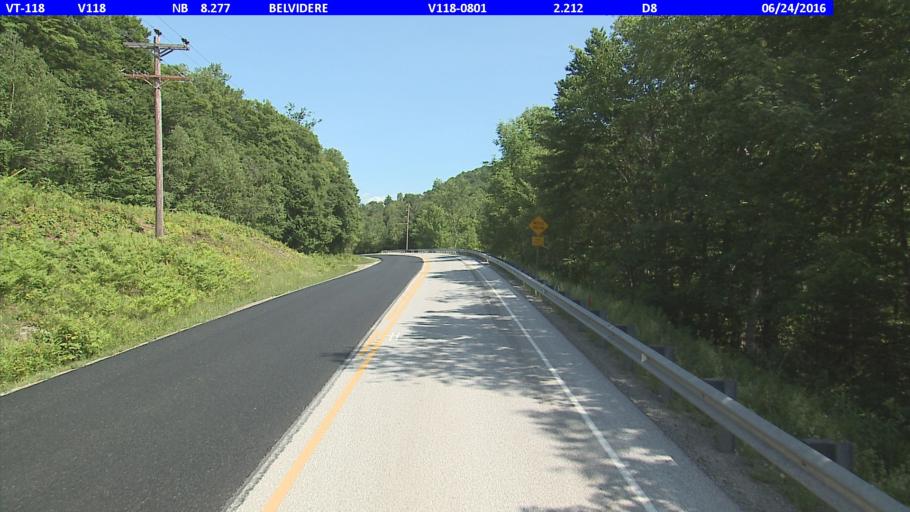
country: US
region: Vermont
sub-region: Lamoille County
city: Johnson
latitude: 44.7913
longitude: -72.6206
